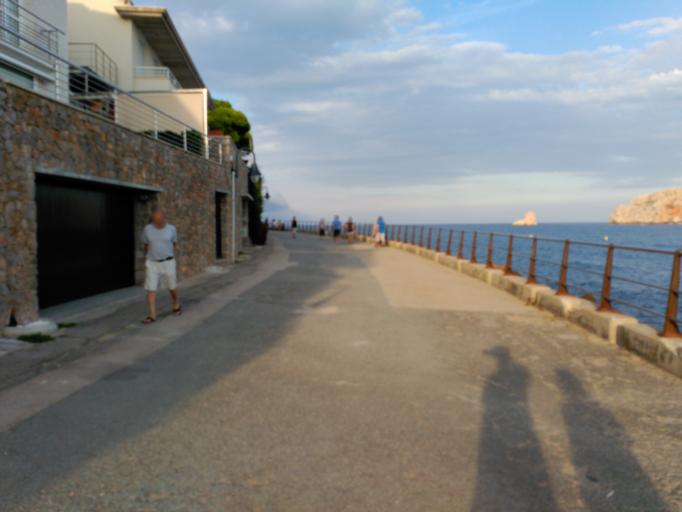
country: ES
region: Catalonia
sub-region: Provincia de Girona
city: Torroella de Montgri
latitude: 42.0532
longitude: 3.2092
